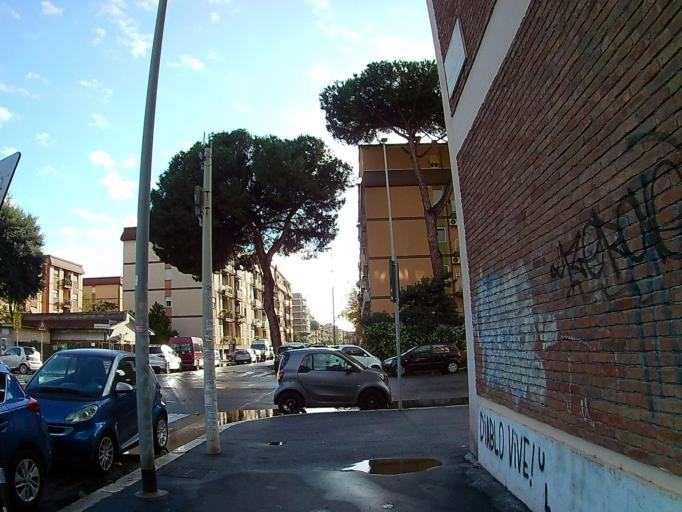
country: IT
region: Latium
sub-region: Citta metropolitana di Roma Capitale
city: Lido di Ostia
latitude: 41.7377
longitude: 12.2875
